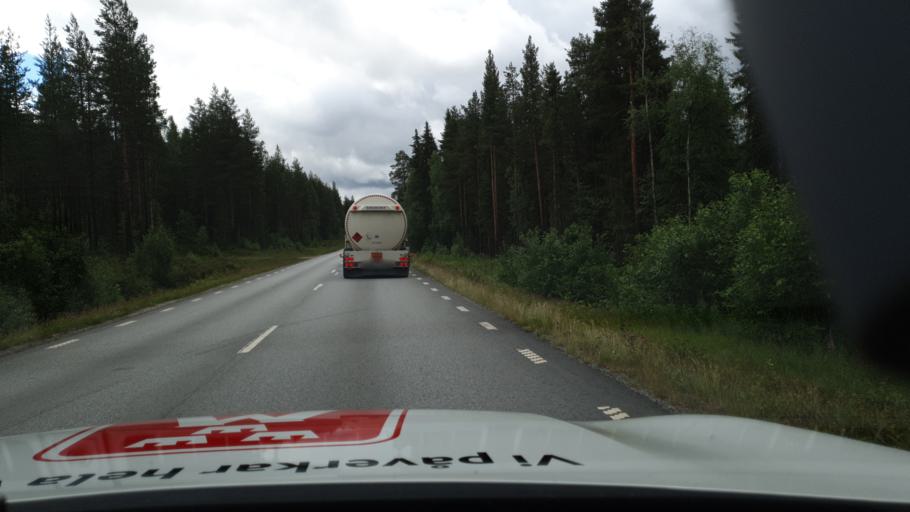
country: SE
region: Vaesterbotten
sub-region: Lycksele Kommun
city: Lycksele
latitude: 64.5605
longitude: 18.7252
